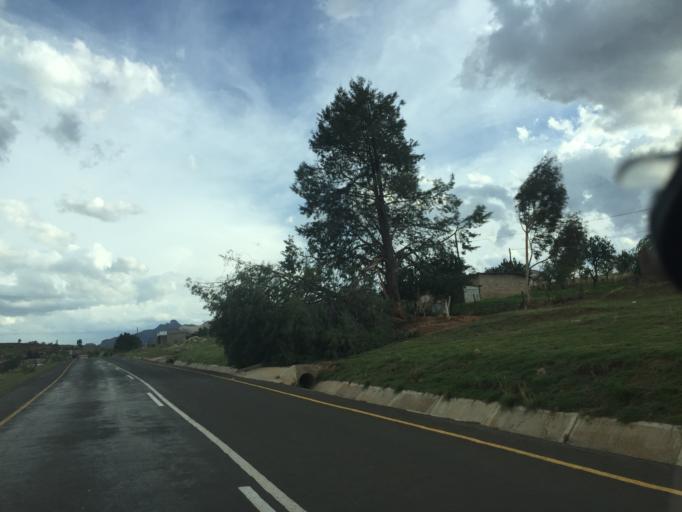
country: LS
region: Berea
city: Teyateyaneng
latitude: -29.1308
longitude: 27.9856
